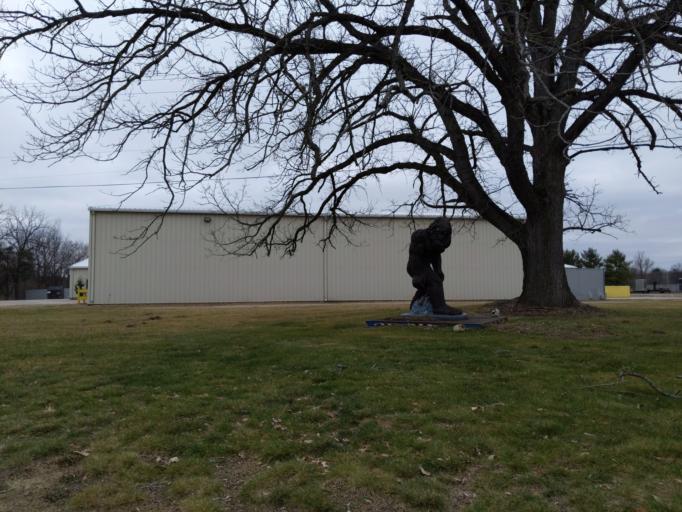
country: US
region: Michigan
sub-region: Ingham County
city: Haslett
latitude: 42.7964
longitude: -84.3520
